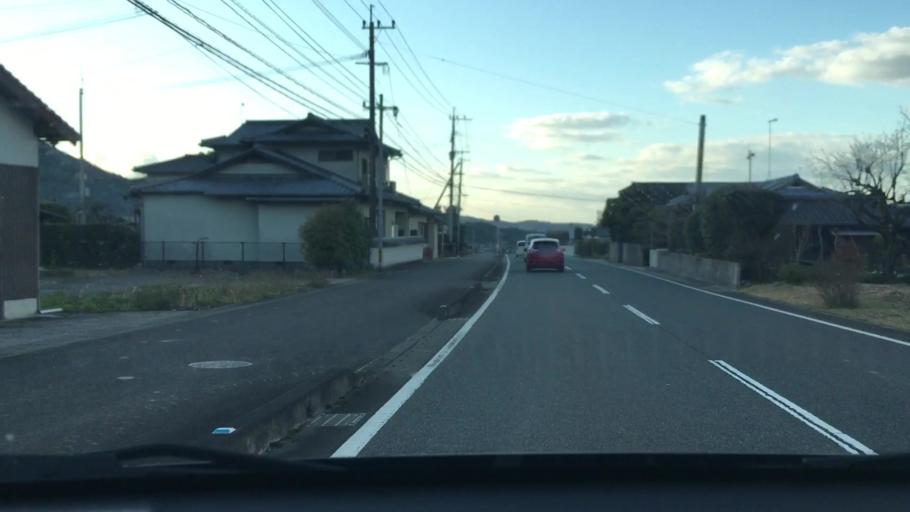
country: JP
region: Oita
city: Bungo-Takada-shi
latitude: 33.5030
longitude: 131.3692
